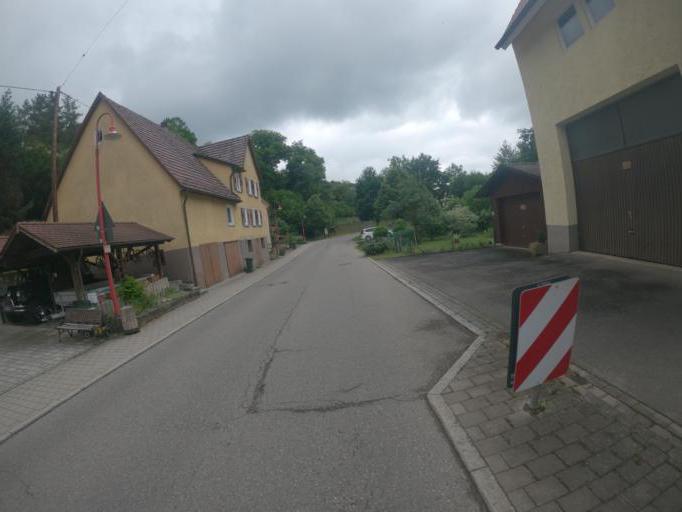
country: DE
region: Baden-Wuerttemberg
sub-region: Regierungsbezirk Stuttgart
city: Ebersbach an der Fils
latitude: 48.7414
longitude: 9.5430
